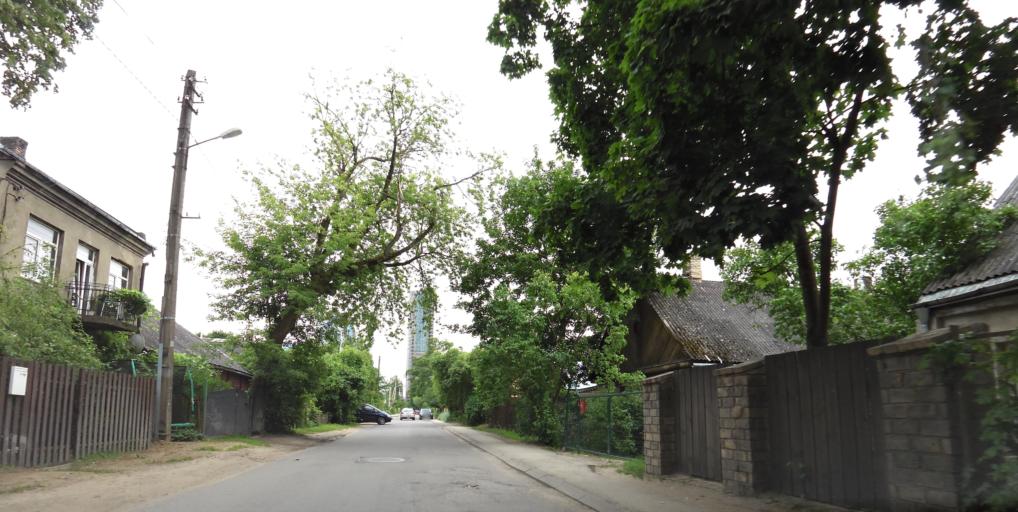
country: LT
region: Vilnius County
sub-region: Vilnius
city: Vilnius
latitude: 54.7011
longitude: 25.2791
